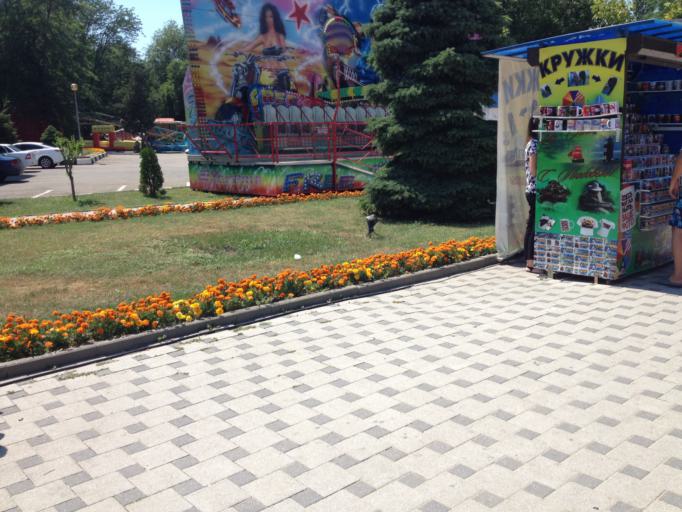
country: RU
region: Krasnodarskiy
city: Anapa
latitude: 44.8961
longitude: 37.3149
